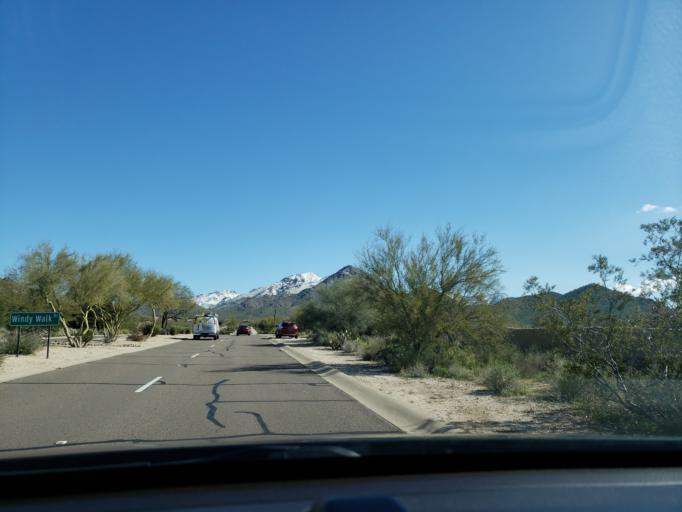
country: US
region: Arizona
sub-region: Maricopa County
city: Carefree
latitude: 33.7115
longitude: -111.8528
